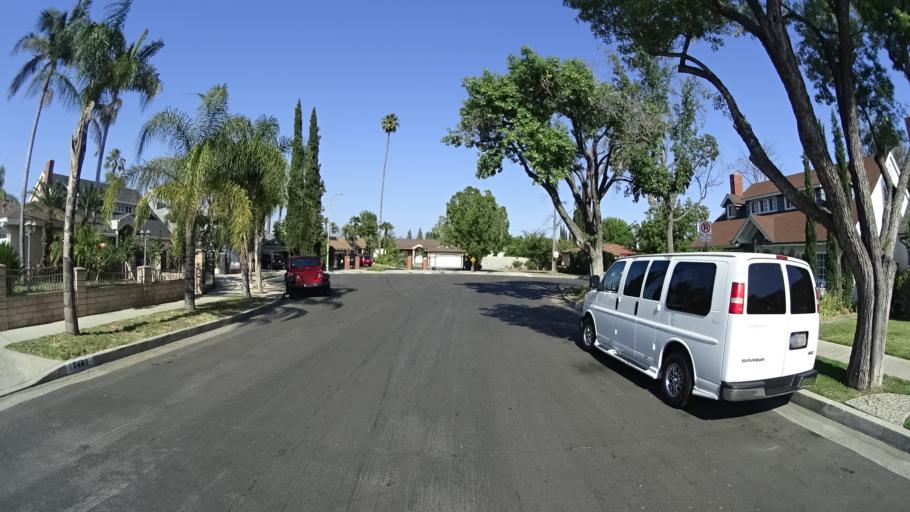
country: US
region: California
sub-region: Los Angeles County
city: Van Nuys
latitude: 34.2189
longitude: -118.4262
